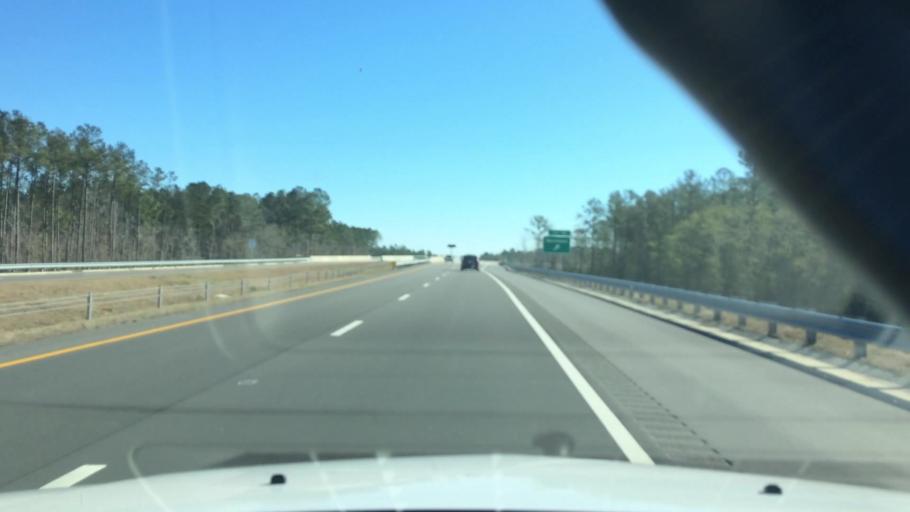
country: US
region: North Carolina
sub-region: Brunswick County
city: Navassa
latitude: 34.2728
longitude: -78.0250
